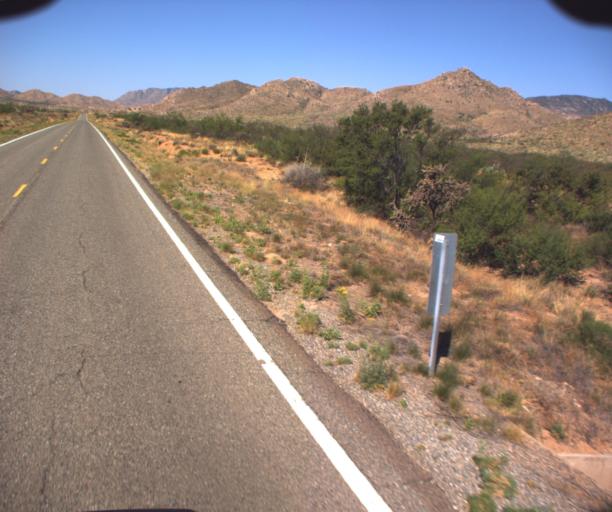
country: US
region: Arizona
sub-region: Graham County
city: Swift Trail Junction
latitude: 32.5899
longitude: -109.6958
